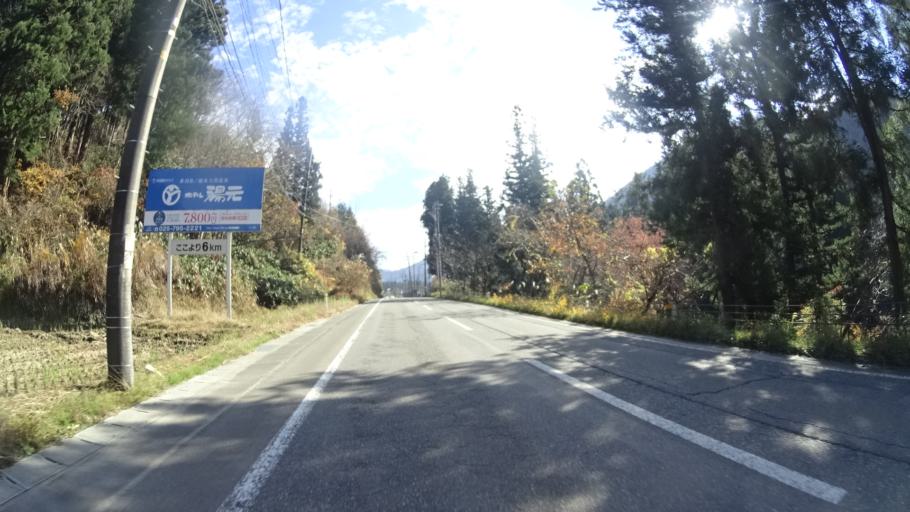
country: JP
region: Niigata
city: Muikamachi
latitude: 37.2228
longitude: 139.0260
